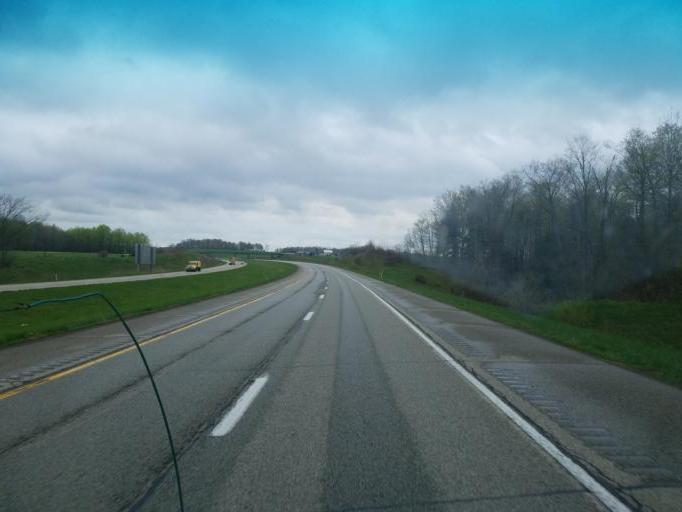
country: US
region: Pennsylvania
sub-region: Erie County
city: North East
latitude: 42.1272
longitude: -79.8031
